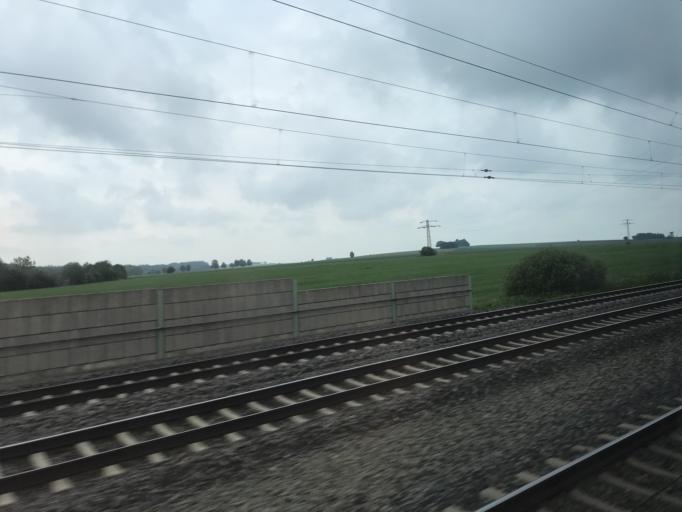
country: DE
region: Bavaria
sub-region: Upper Bavaria
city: Althegnenberg
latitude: 48.2387
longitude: 11.0574
